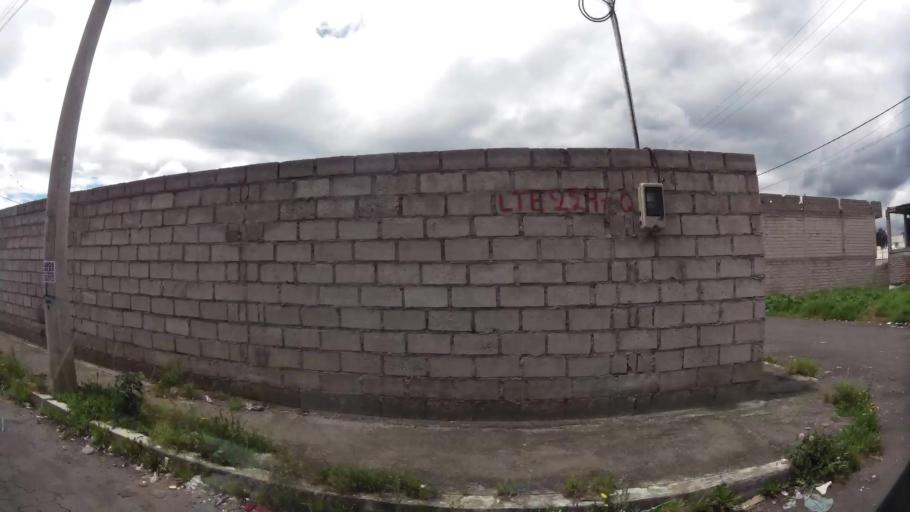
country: EC
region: Pichincha
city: Sangolqui
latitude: -0.3336
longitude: -78.5359
